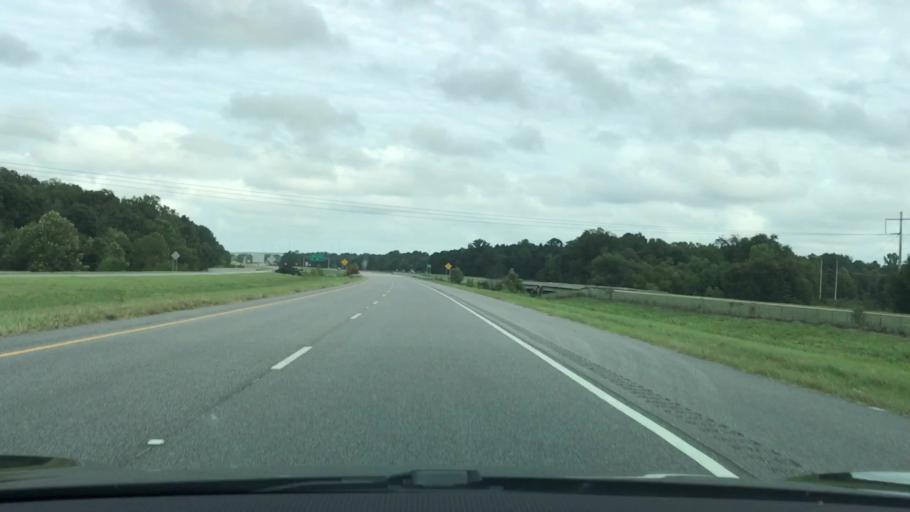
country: US
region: Alabama
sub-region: Montgomery County
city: Pike Road
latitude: 32.3536
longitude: -86.0678
